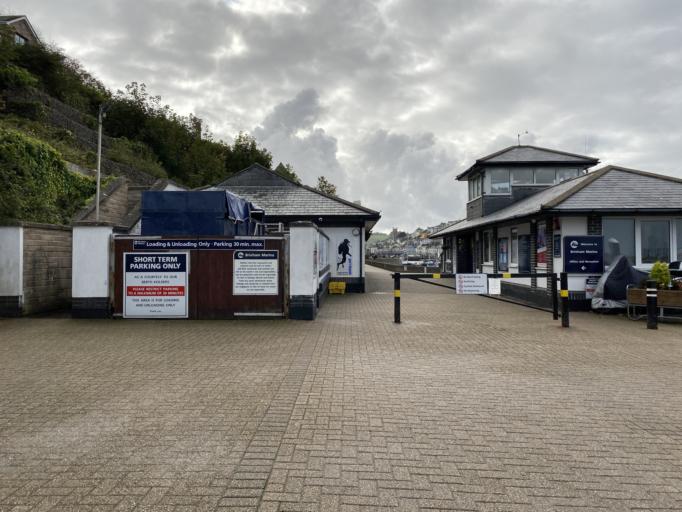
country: GB
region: England
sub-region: Borough of Torbay
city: Brixham
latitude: 50.3991
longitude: -3.5061
